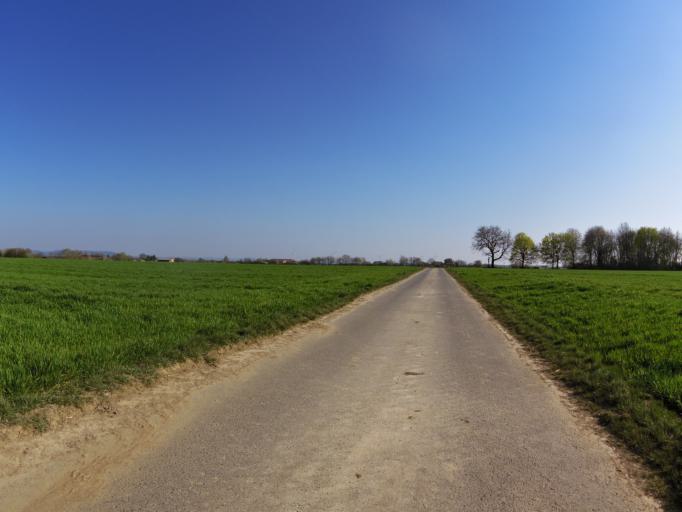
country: DE
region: Bavaria
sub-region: Regierungsbezirk Unterfranken
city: Oberpleichfeld
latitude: 49.8263
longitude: 10.0905
